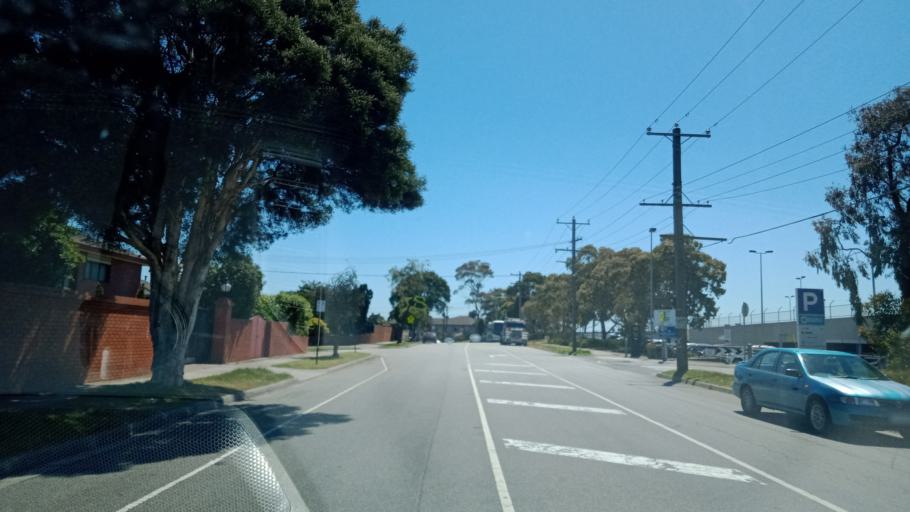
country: AU
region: Victoria
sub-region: Greater Dandenong
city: Noble Park North
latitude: -37.9350
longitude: 145.1879
